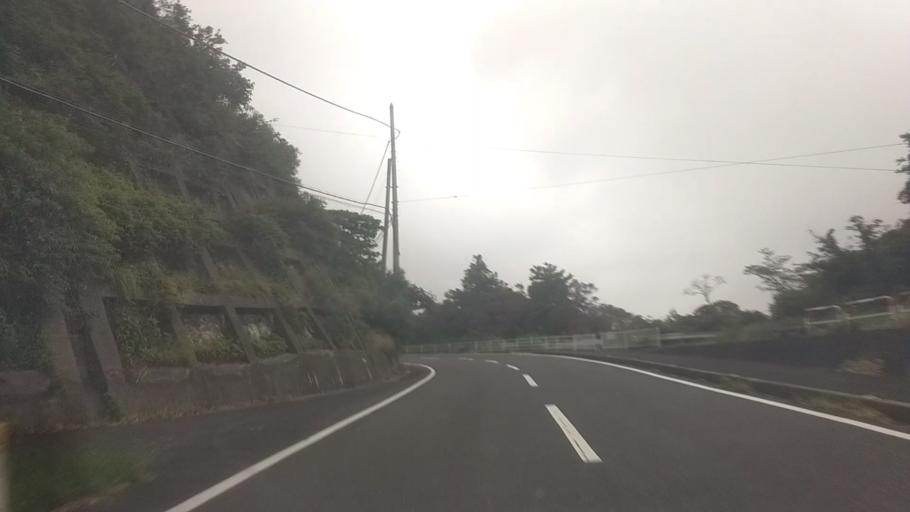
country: JP
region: Chiba
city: Kawaguchi
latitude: 35.1427
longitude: 140.1501
